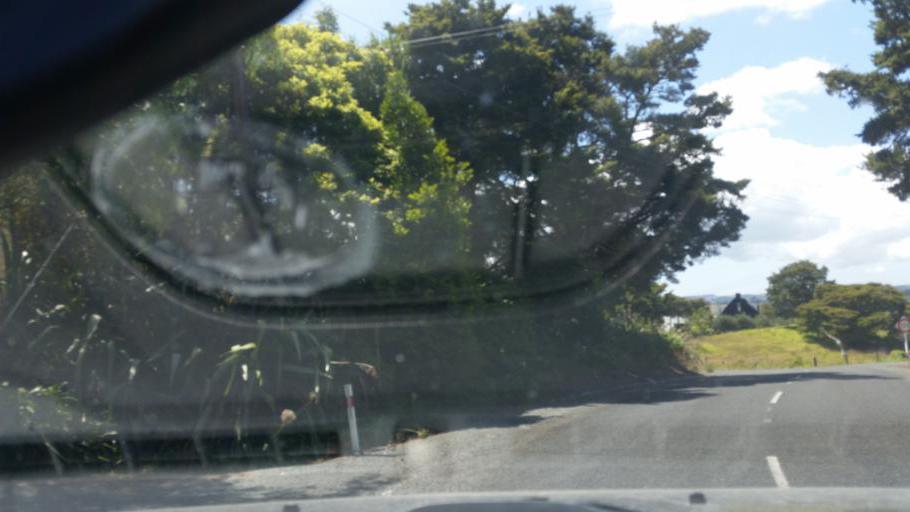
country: NZ
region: Northland
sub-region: Whangarei
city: Ruakaka
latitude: -36.1386
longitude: 174.2252
